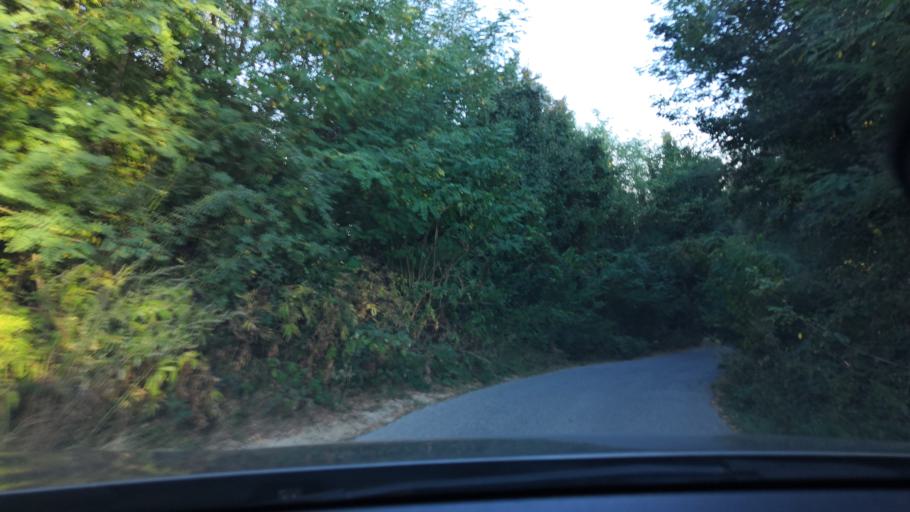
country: RS
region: Central Serbia
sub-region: Sumadijski Okrug
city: Arangelovac
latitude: 44.3291
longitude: 20.5815
